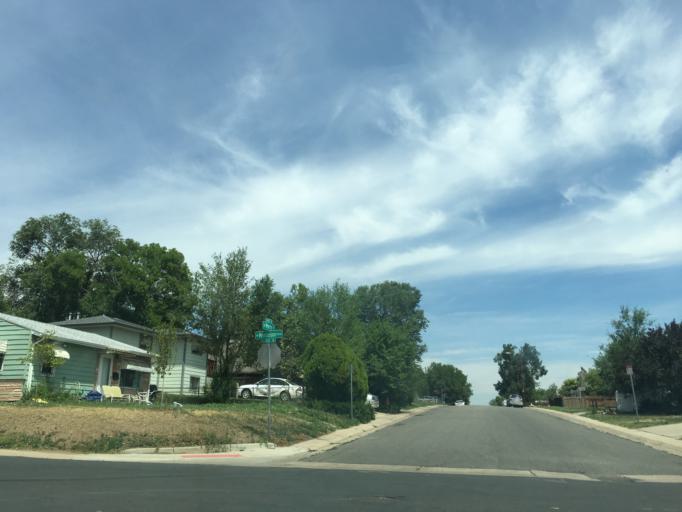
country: US
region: Colorado
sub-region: Jefferson County
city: Lakewood
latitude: 39.6966
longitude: -105.0402
